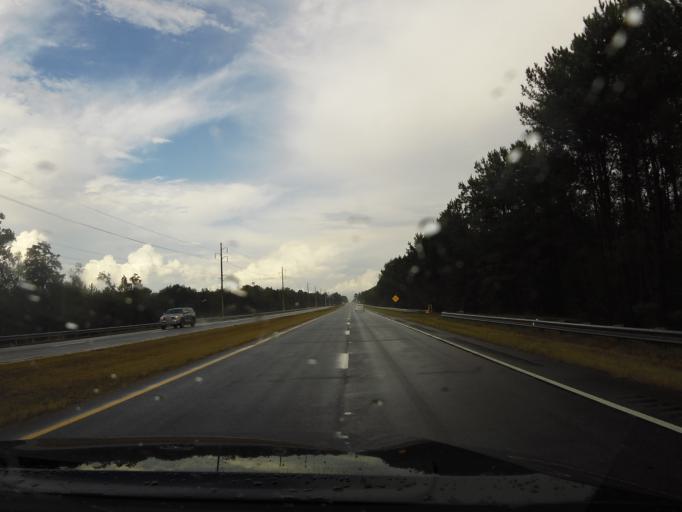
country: US
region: Georgia
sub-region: Long County
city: Ludowici
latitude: 31.7035
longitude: -81.7639
